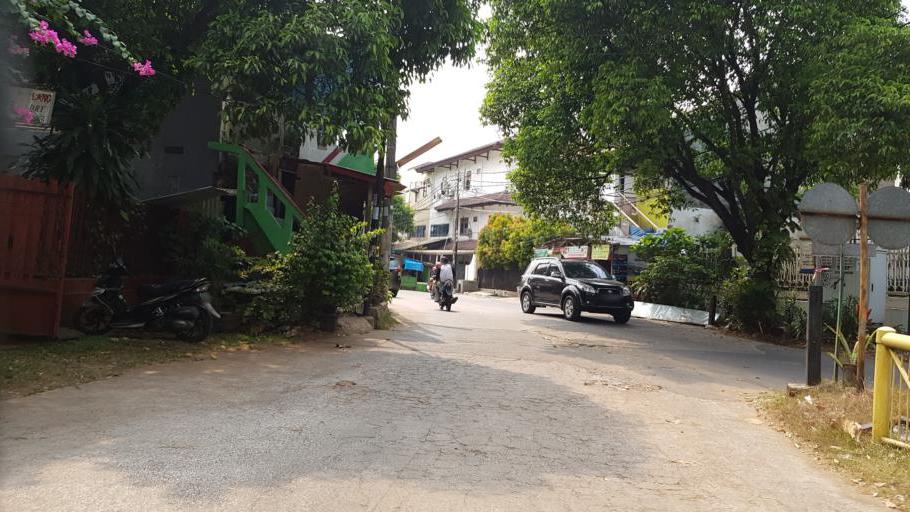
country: ID
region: West Java
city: Pamulang
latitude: -6.3268
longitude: 106.7859
